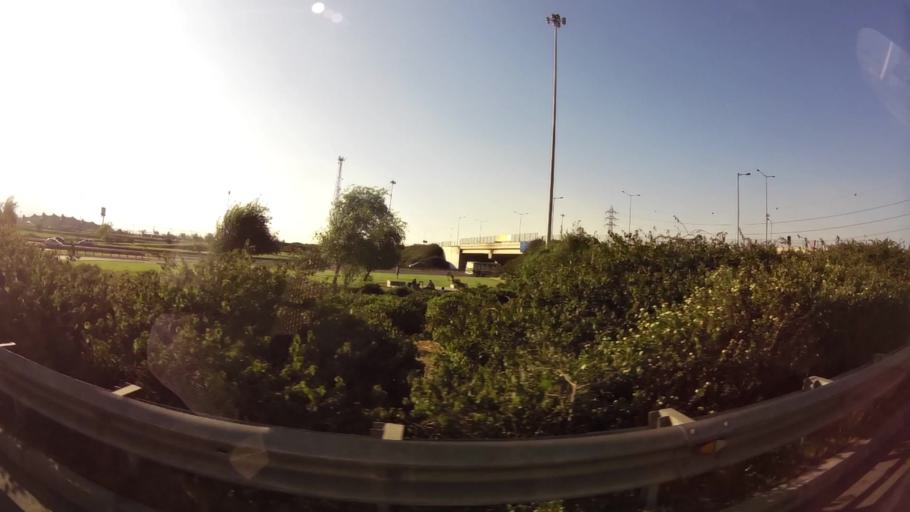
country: CL
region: Santiago Metropolitan
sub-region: Provincia de Santiago
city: Lo Prado
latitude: -33.4919
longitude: -70.7492
